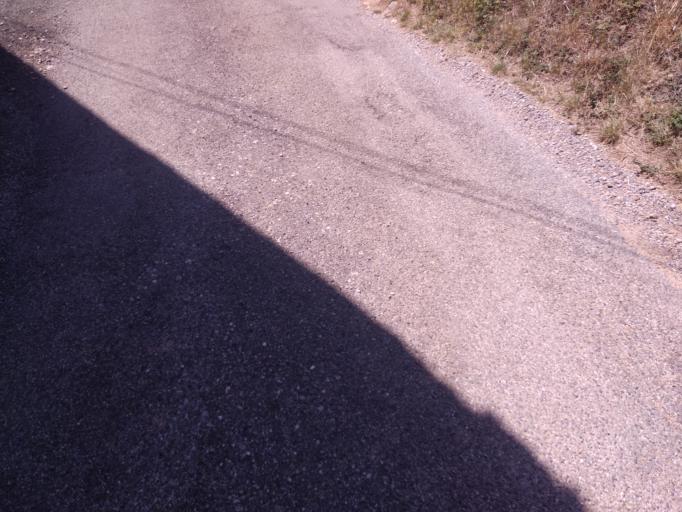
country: FR
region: Rhone-Alpes
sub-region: Departement de l'Ardeche
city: Sarras
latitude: 45.1873
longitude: 4.7864
